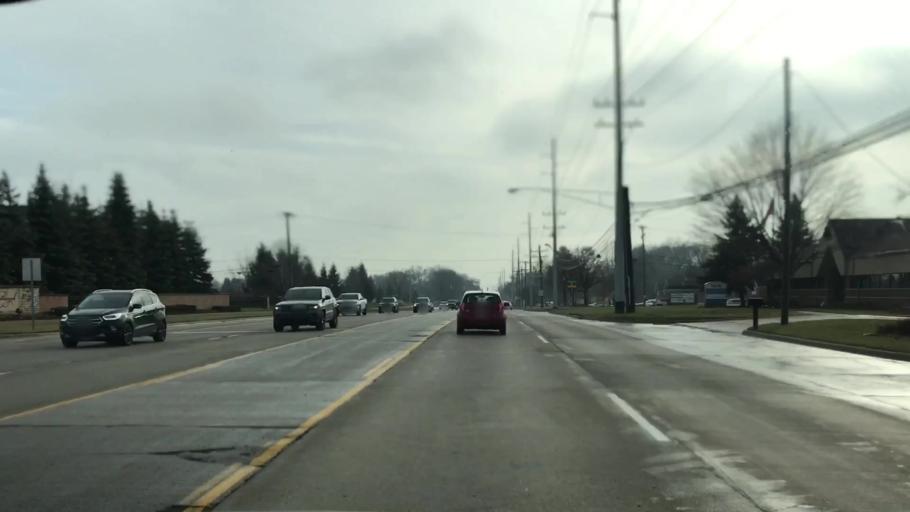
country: US
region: Michigan
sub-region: Oakland County
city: Troy
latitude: 42.6180
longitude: -83.1304
